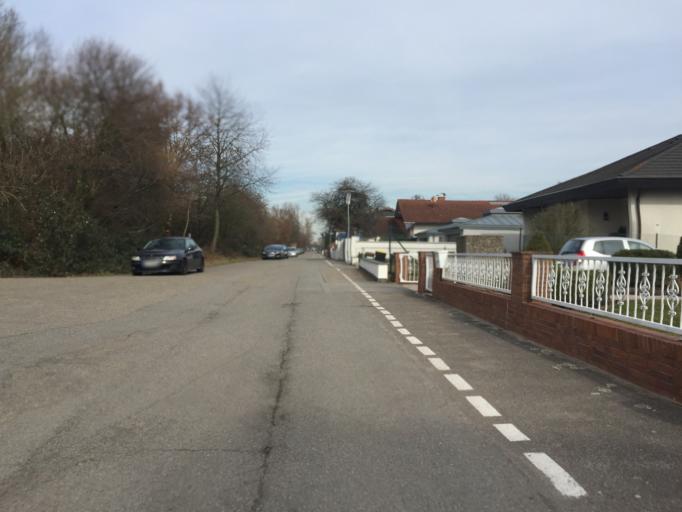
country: DE
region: Hesse
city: Viernheim
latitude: 49.5274
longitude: 8.5929
